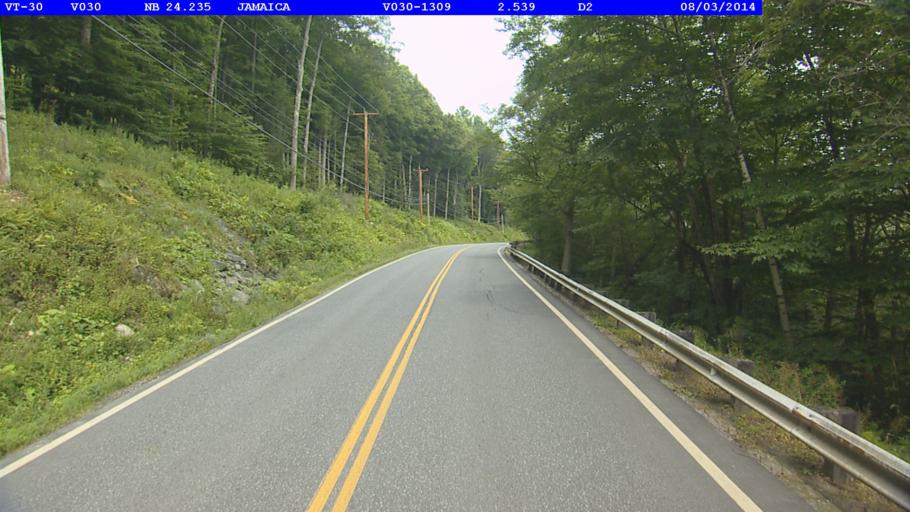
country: US
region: Vermont
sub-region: Windham County
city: Dover
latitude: 43.0874
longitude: -72.7661
